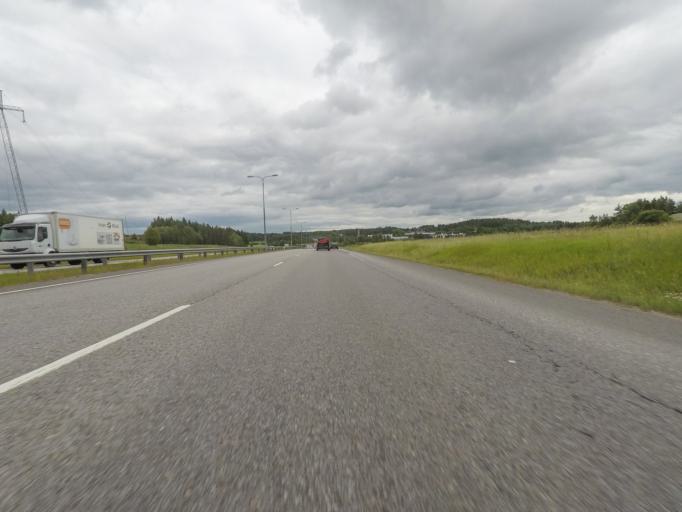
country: FI
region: Varsinais-Suomi
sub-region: Turku
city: Kaarina
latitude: 60.4754
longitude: 22.3485
